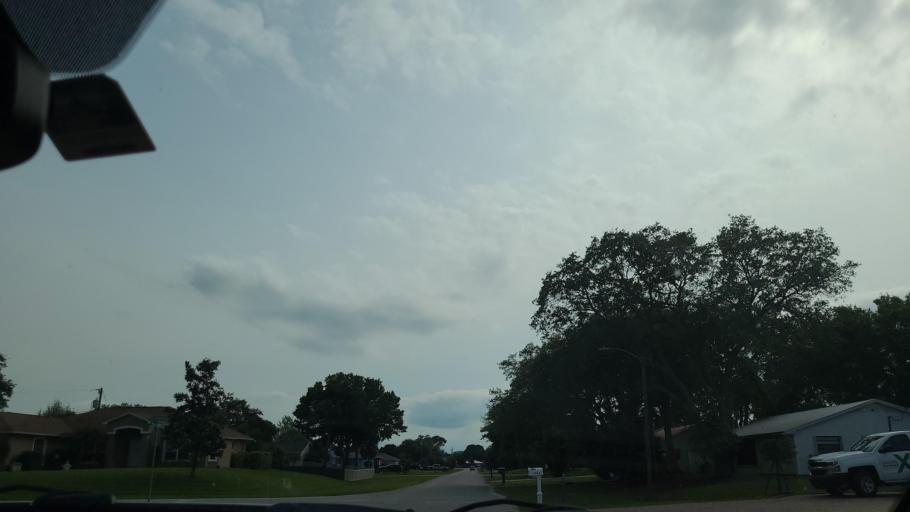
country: US
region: Florida
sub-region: Indian River County
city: Sebastian
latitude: 27.7854
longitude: -80.4876
